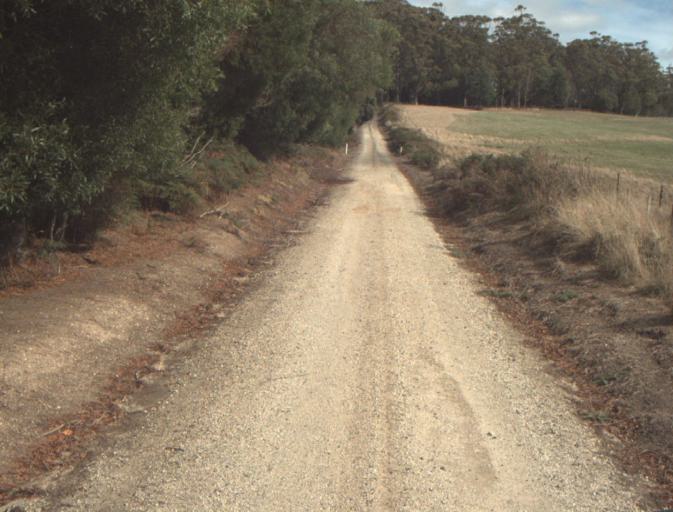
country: AU
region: Tasmania
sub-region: Launceston
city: Mayfield
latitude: -41.1811
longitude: 147.1943
